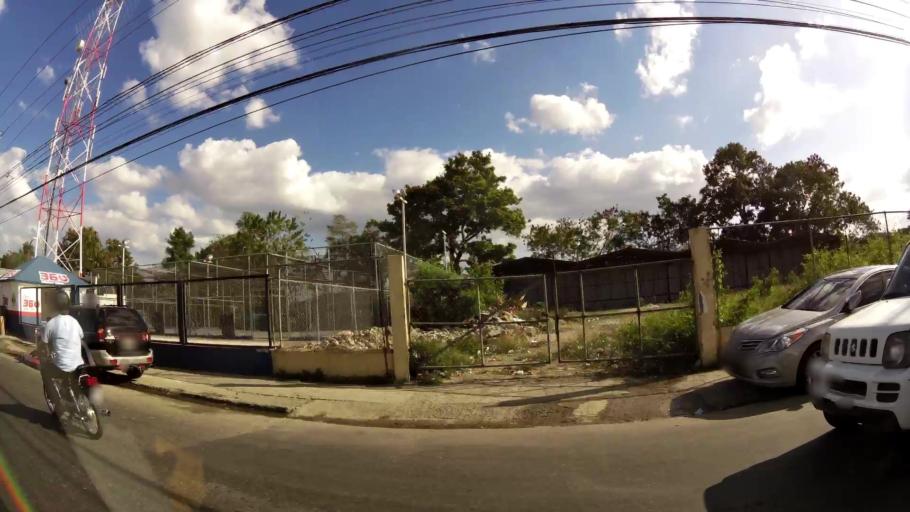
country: DO
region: Nacional
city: Santo Domingo
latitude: 18.5066
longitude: -69.9844
